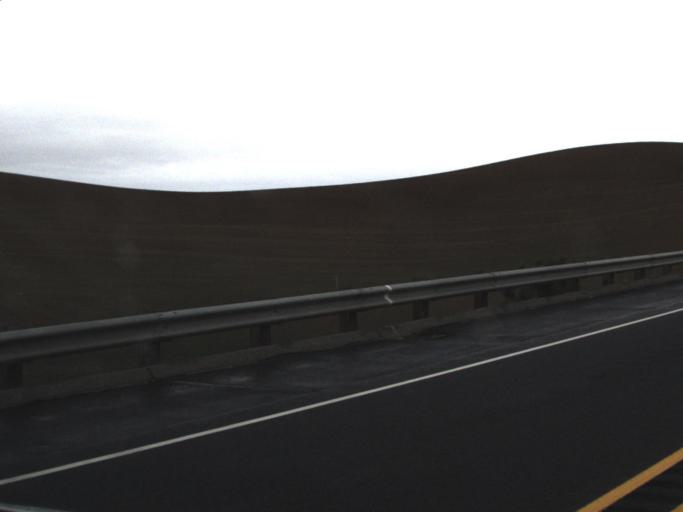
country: US
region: Washington
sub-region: Whitman County
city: Pullman
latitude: 46.7223
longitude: -117.2216
